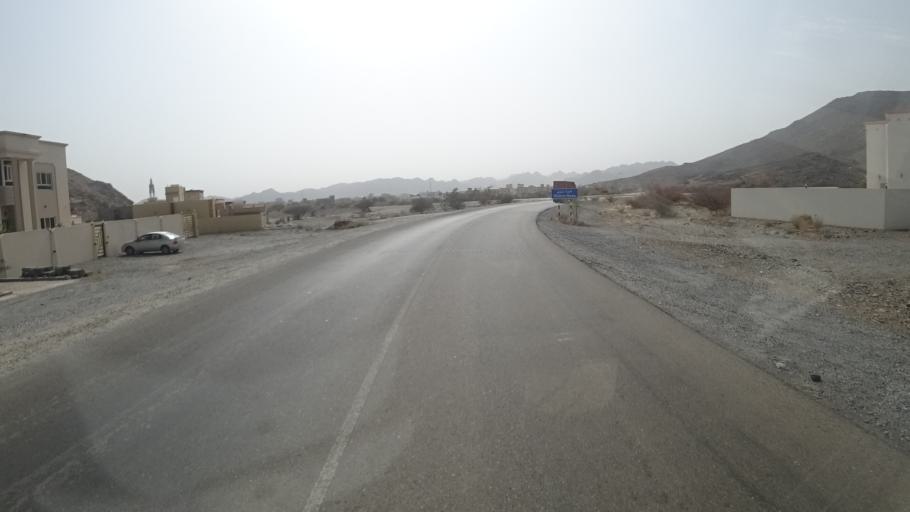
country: OM
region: Muhafazat ad Dakhiliyah
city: Nizwa
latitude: 23.0019
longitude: 57.5618
